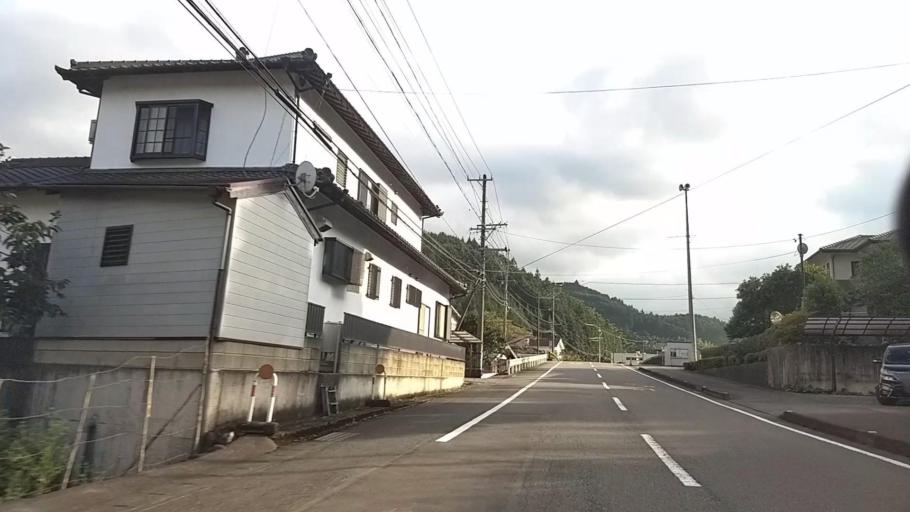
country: JP
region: Shizuoka
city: Fujinomiya
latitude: 35.1829
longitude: 138.5458
